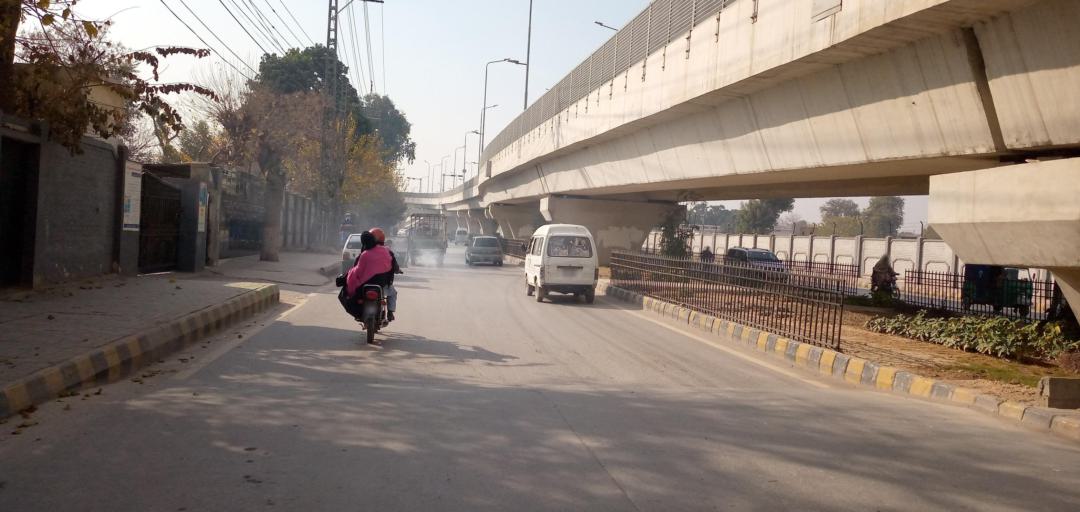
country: PK
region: Khyber Pakhtunkhwa
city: Peshawar
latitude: 34.0039
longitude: 71.5312
